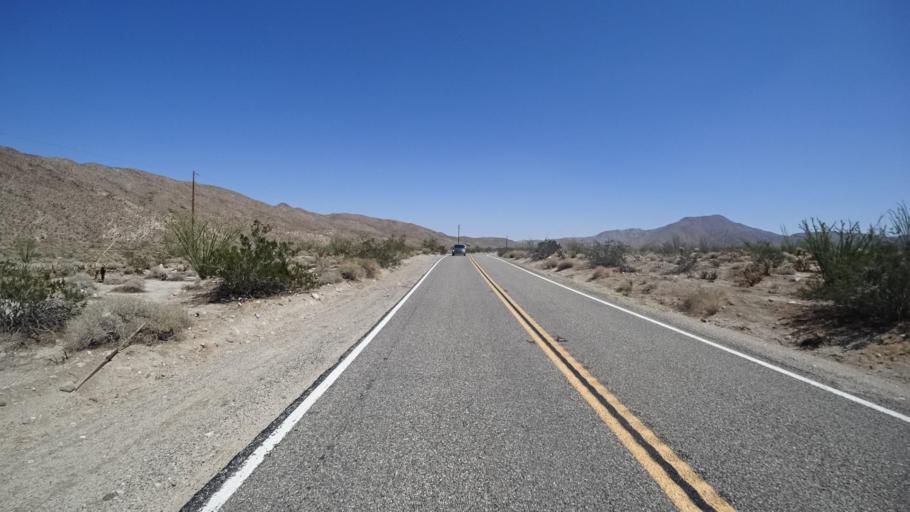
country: US
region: California
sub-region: San Diego County
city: Borrego Springs
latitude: 33.1355
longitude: -116.3548
